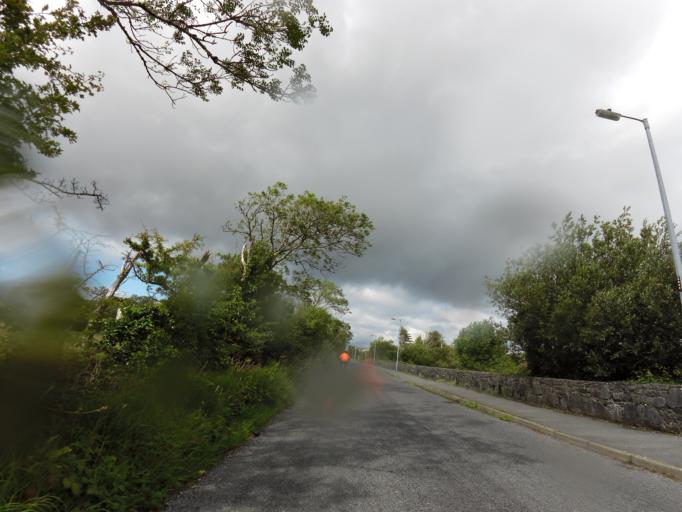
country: IE
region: Connaught
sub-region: County Galway
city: Oughterard
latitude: 53.4253
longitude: -9.3273
